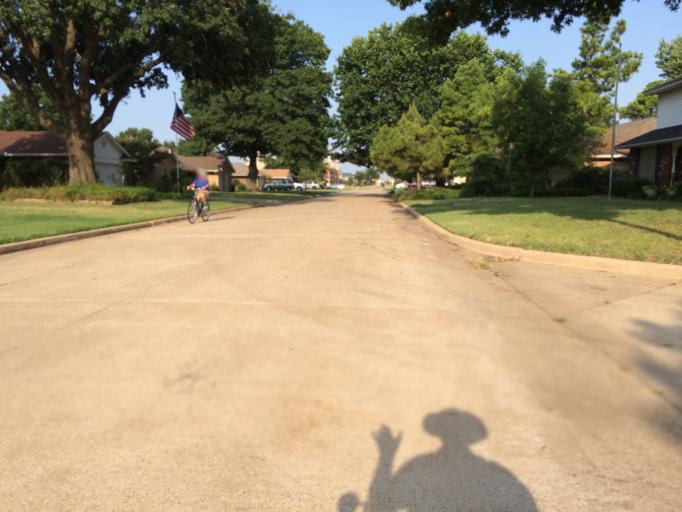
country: US
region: Oklahoma
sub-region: Cleveland County
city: Norman
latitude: 35.2261
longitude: -97.4746
